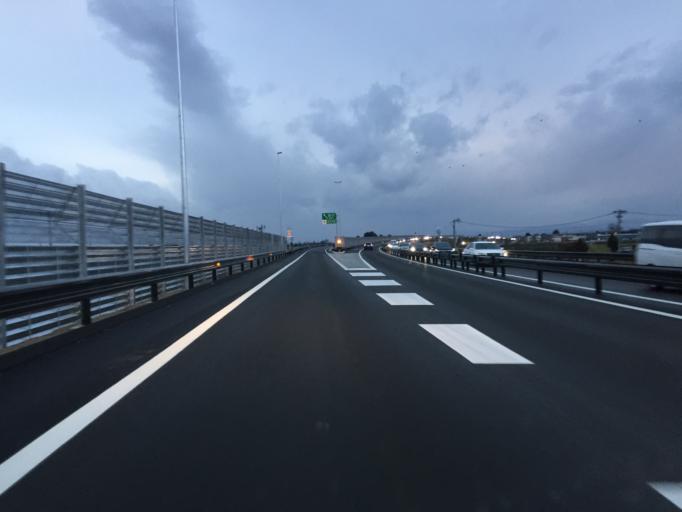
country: JP
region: Yamagata
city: Yonezawa
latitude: 37.9174
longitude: 140.1372
